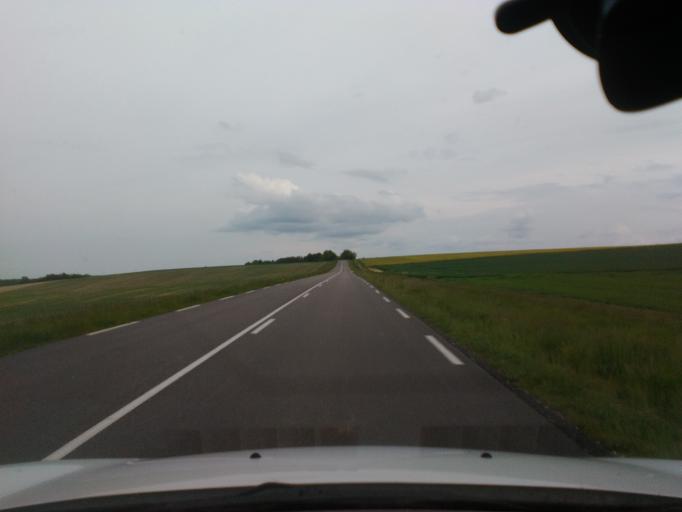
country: FR
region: Champagne-Ardenne
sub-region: Departement de la Haute-Marne
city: Lavilleneuve-au-Roi
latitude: 48.2007
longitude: 4.9416
